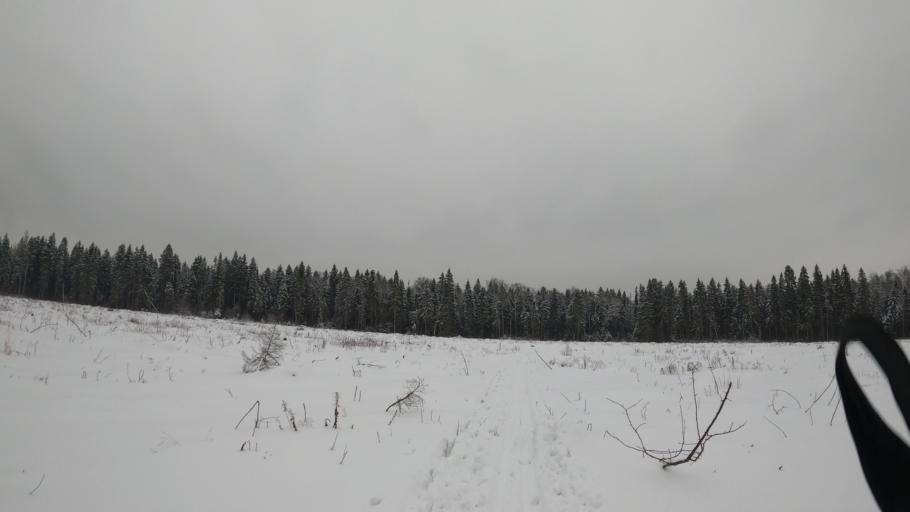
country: RU
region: Moskovskaya
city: Firsanovka
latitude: 55.9623
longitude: 37.2232
